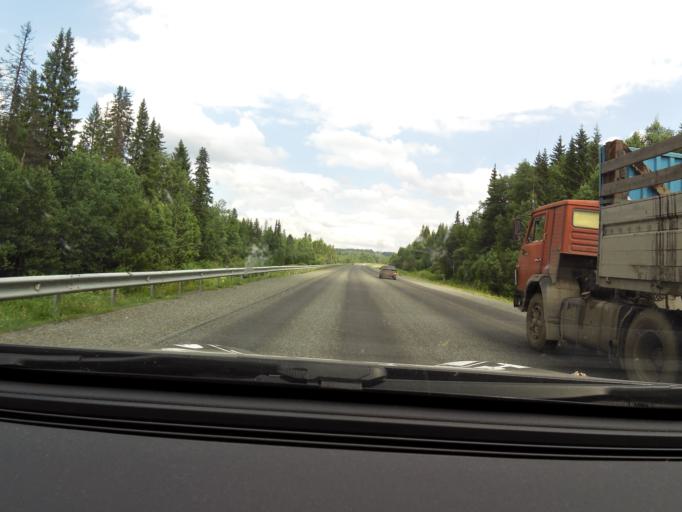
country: RU
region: Sverdlovsk
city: Arti
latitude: 56.7939
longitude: 58.4589
